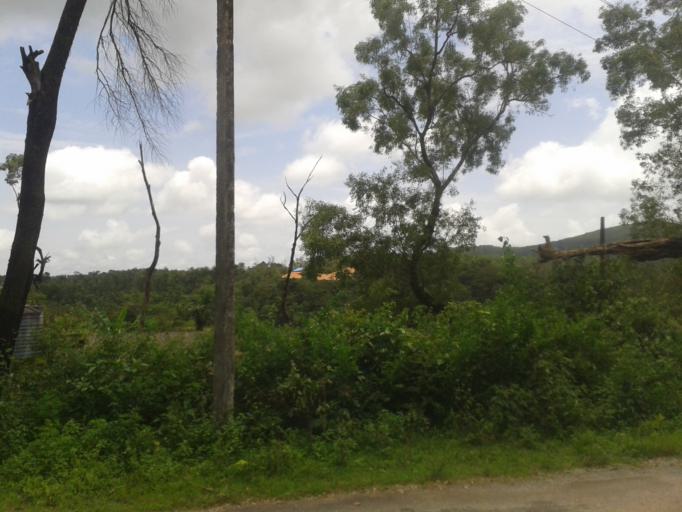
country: IN
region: Karnataka
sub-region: Chikmagalur
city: Mudigere
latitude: 12.9871
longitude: 75.6272
